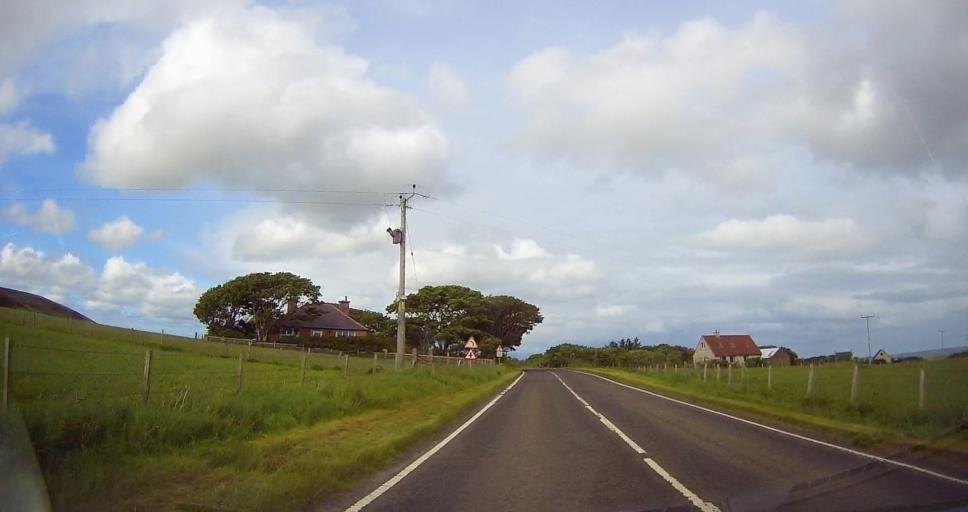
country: GB
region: Scotland
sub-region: Orkney Islands
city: Orkney
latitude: 59.0215
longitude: -3.0989
